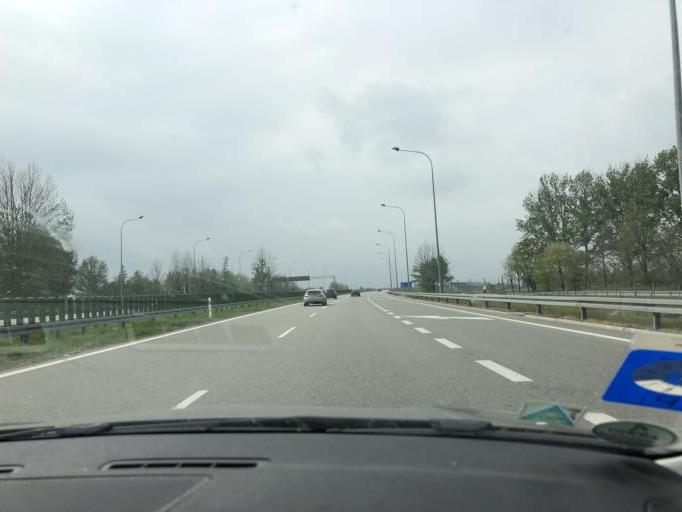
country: PL
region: Subcarpathian Voivodeship
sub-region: Powiat debicki
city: Brzeznica
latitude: 50.0796
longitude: 21.4689
